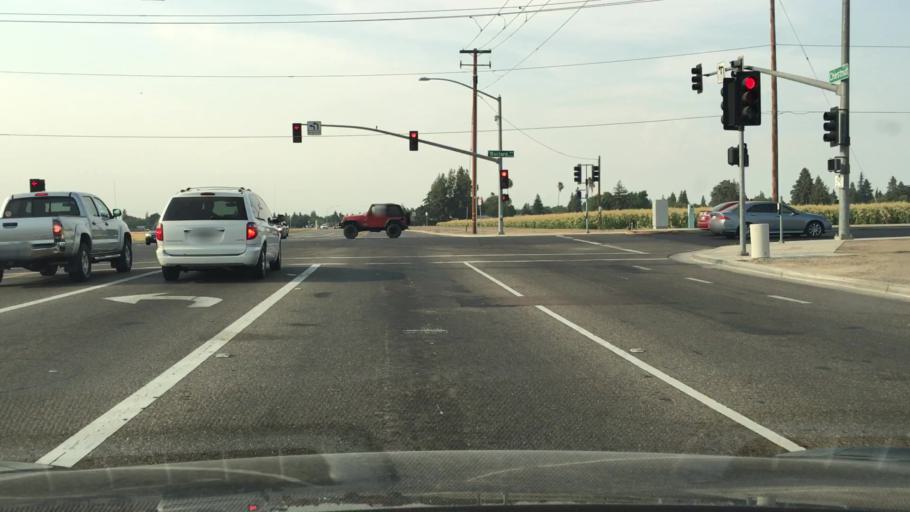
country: US
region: California
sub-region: Fresno County
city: Clovis
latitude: 36.8227
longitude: -119.7360
